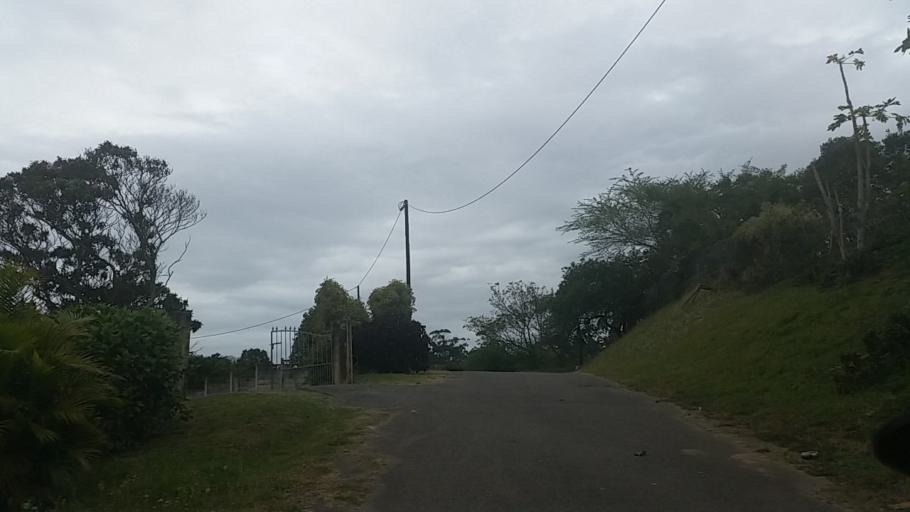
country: ZA
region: KwaZulu-Natal
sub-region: eThekwini Metropolitan Municipality
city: Berea
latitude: -29.8432
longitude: 30.9421
